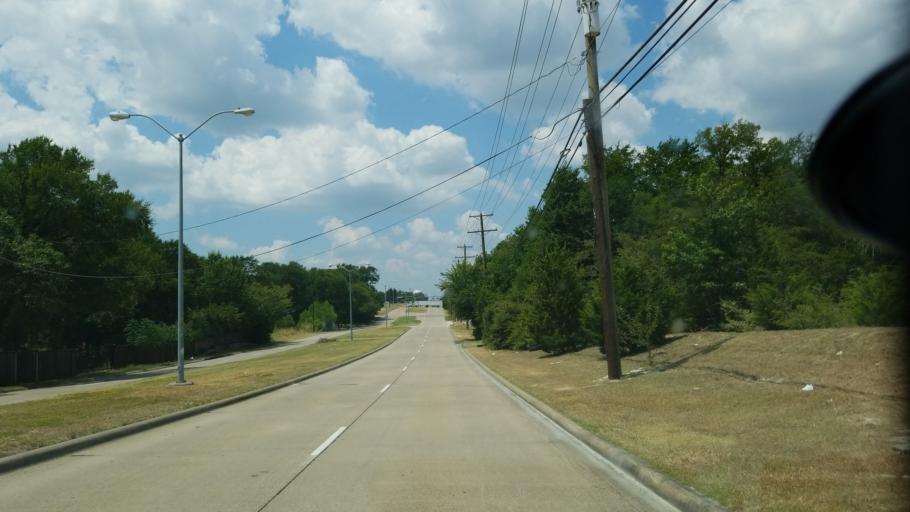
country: US
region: Texas
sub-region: Dallas County
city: Duncanville
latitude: 32.6767
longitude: -96.8866
